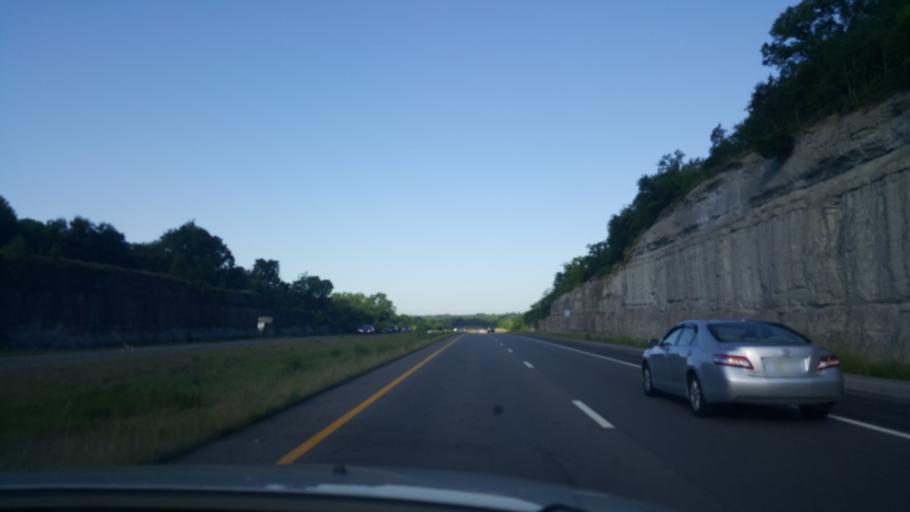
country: US
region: Tennessee
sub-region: Maury County
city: Columbia
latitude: 35.6275
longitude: -87.1070
